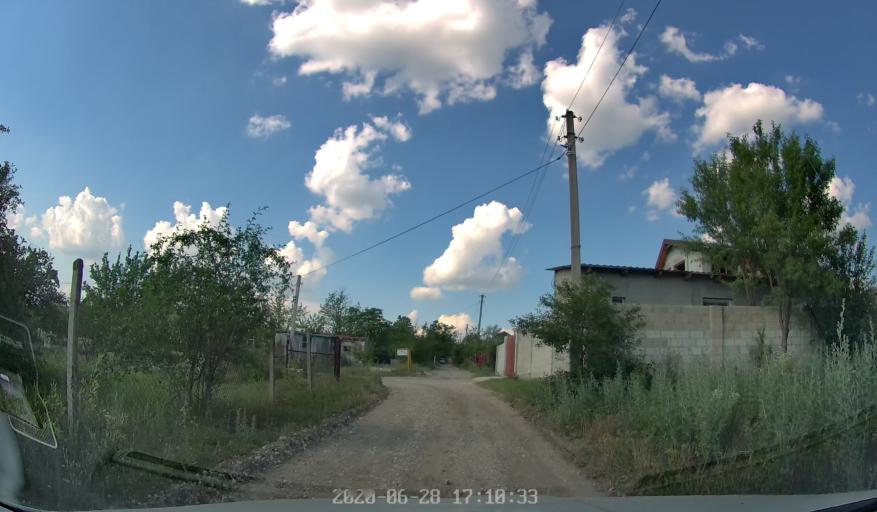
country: MD
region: Laloveni
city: Ialoveni
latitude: 46.9863
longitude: 28.7005
